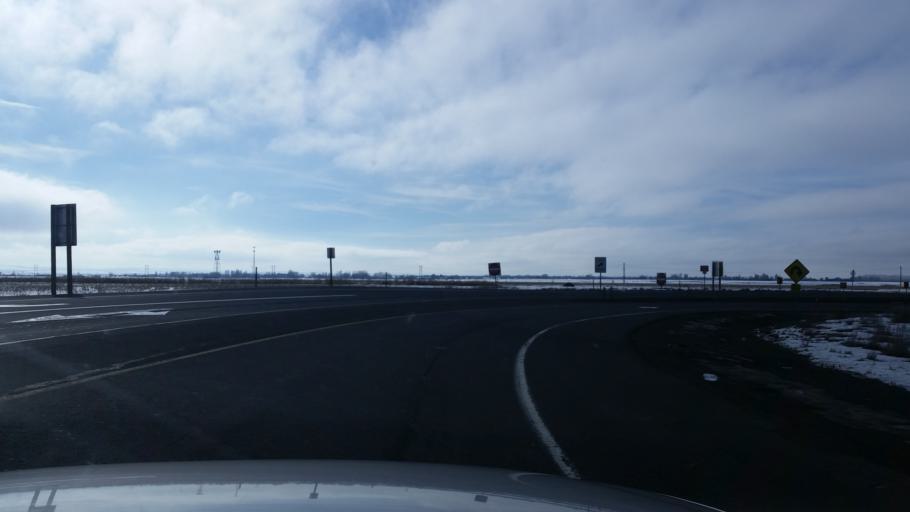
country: US
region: Washington
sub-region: Grant County
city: Moses Lake
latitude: 47.0977
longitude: -119.2431
